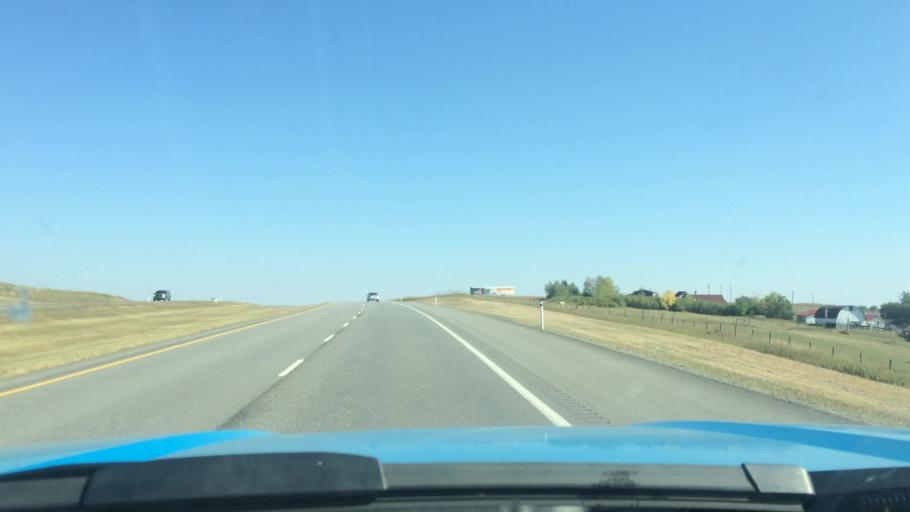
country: CA
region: Alberta
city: Cochrane
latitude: 51.0912
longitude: -114.5771
